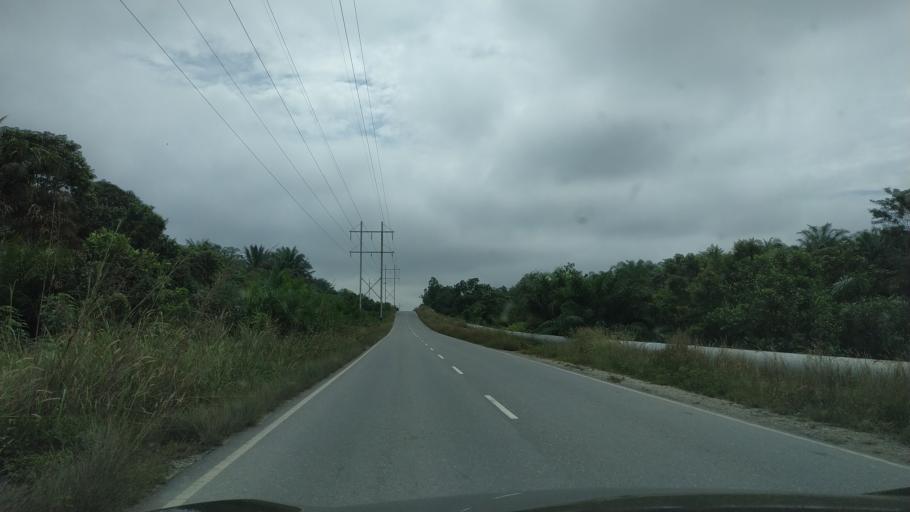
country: ID
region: Riau
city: Pekanbaru
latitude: 0.6435
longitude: 101.6732
